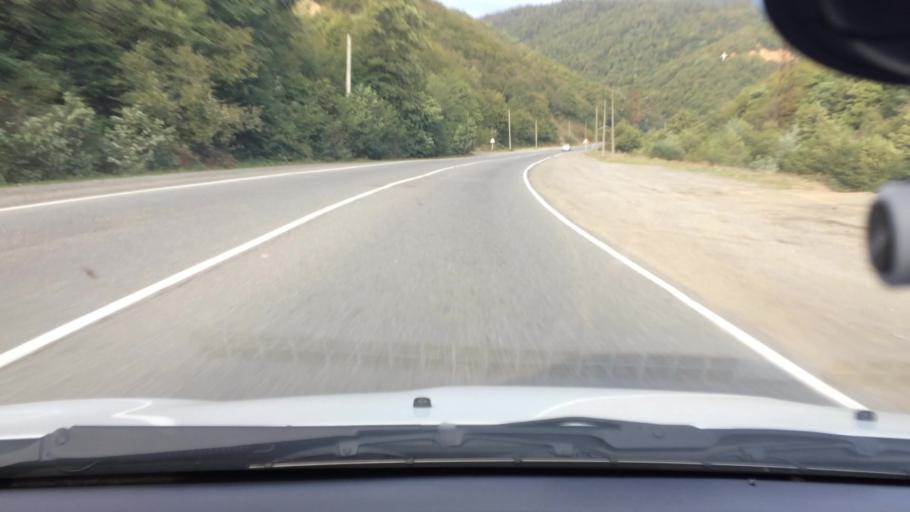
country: GE
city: Surami
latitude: 42.0403
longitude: 43.5076
